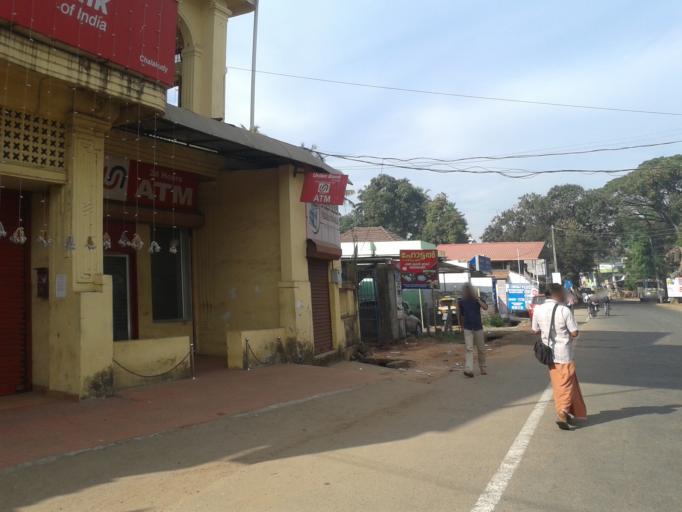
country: IN
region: Kerala
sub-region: Thrissur District
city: Kizhake Chalakudi
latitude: 10.3077
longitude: 76.3369
